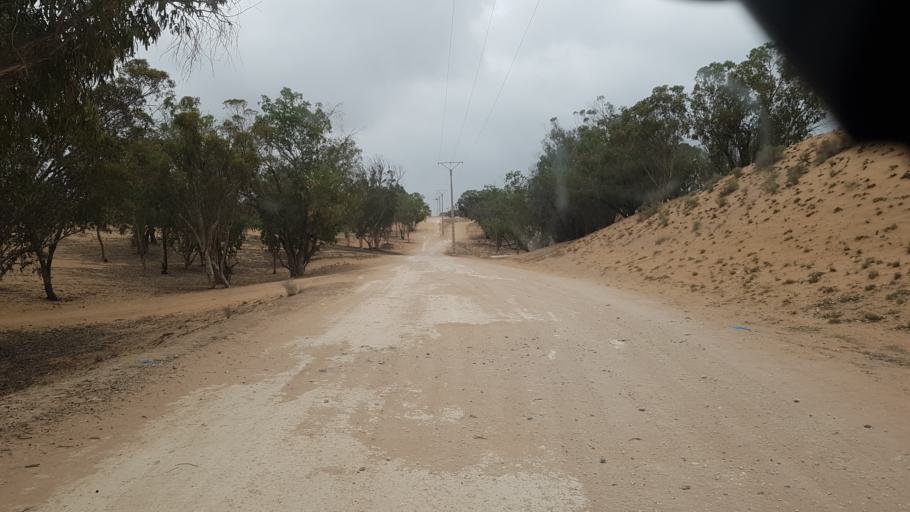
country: MA
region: Souss-Massa-Draa
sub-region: Inezgane-Ait Mellou
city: Inezgane
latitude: 30.3154
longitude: -9.5384
